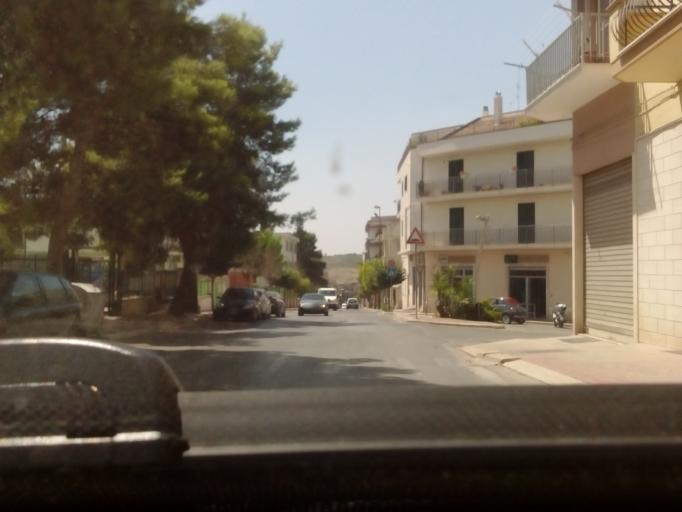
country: IT
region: Apulia
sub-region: Provincia di Bari
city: Gravina in Puglia
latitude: 40.8153
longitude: 16.4219
